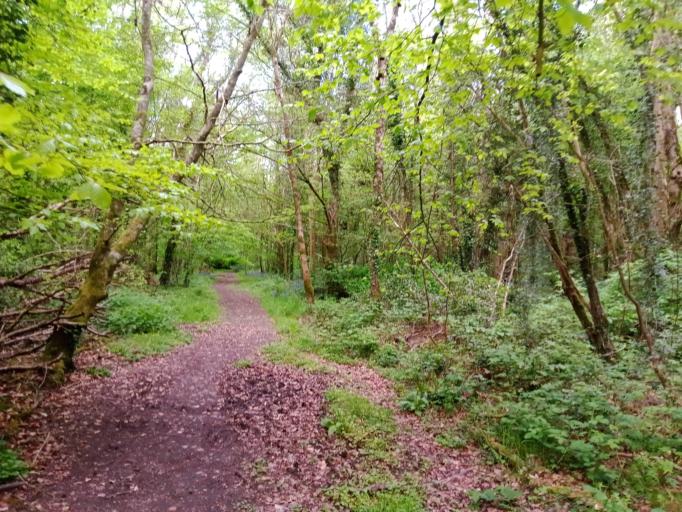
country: IE
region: Leinster
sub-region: Kilkenny
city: Castlecomer
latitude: 52.8198
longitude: -7.2057
